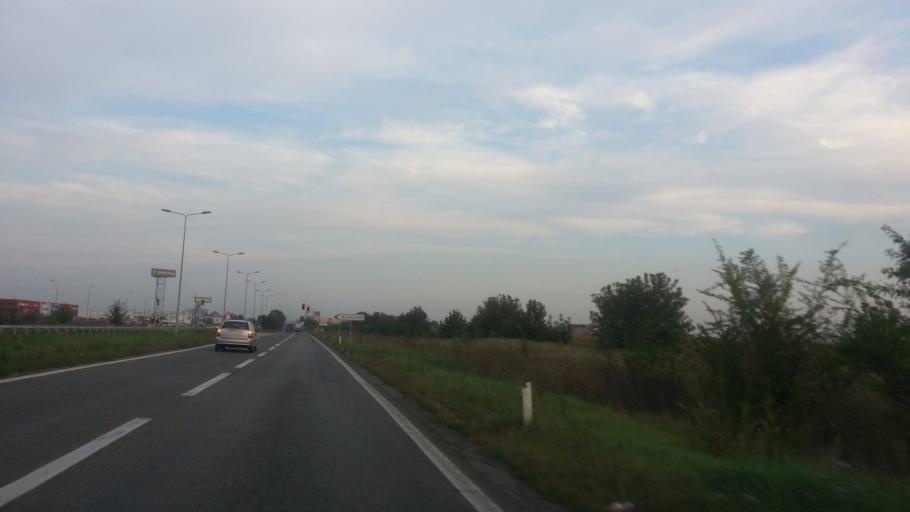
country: RS
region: Central Serbia
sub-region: Belgrade
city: Zemun
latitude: 44.8678
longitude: 20.3409
